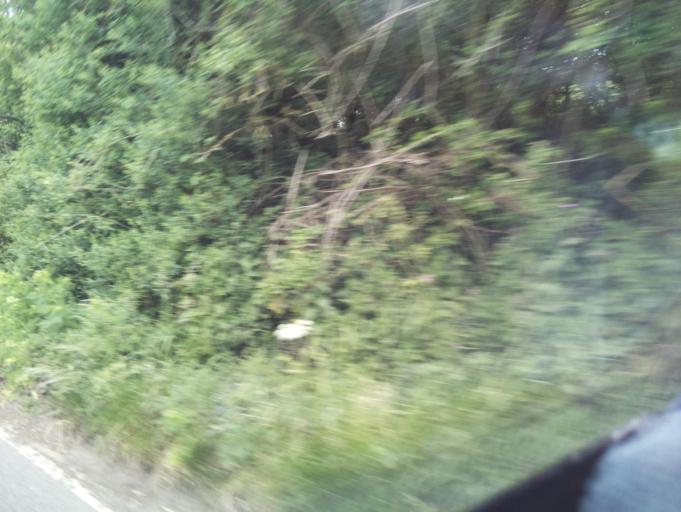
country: GB
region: England
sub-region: Dorset
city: Sherborne
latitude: 50.9915
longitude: -2.5035
